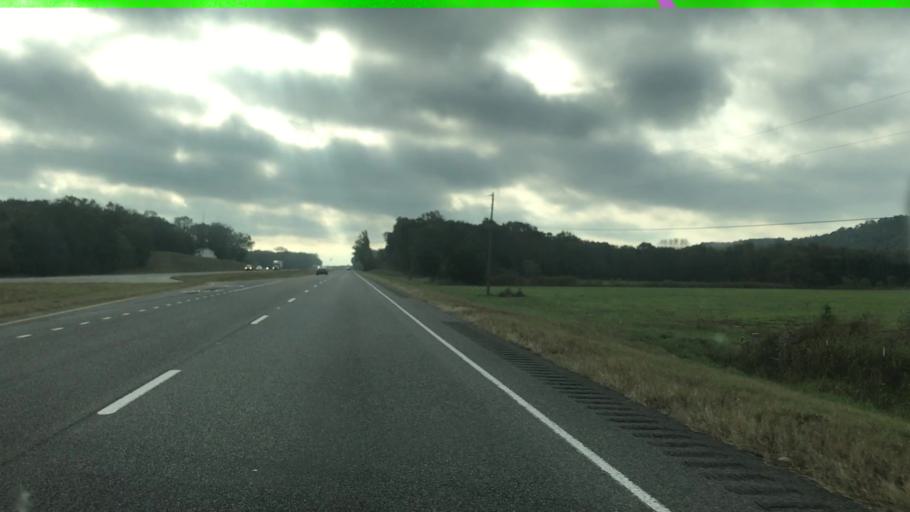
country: US
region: Alabama
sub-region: Morgan County
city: Danville
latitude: 34.4050
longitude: -87.1404
